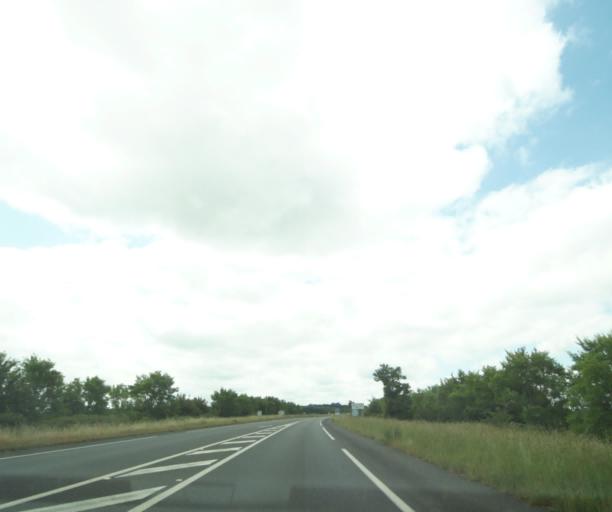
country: FR
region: Poitou-Charentes
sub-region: Departement des Deux-Sevres
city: Saint-Varent
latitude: 46.8737
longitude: -0.1974
